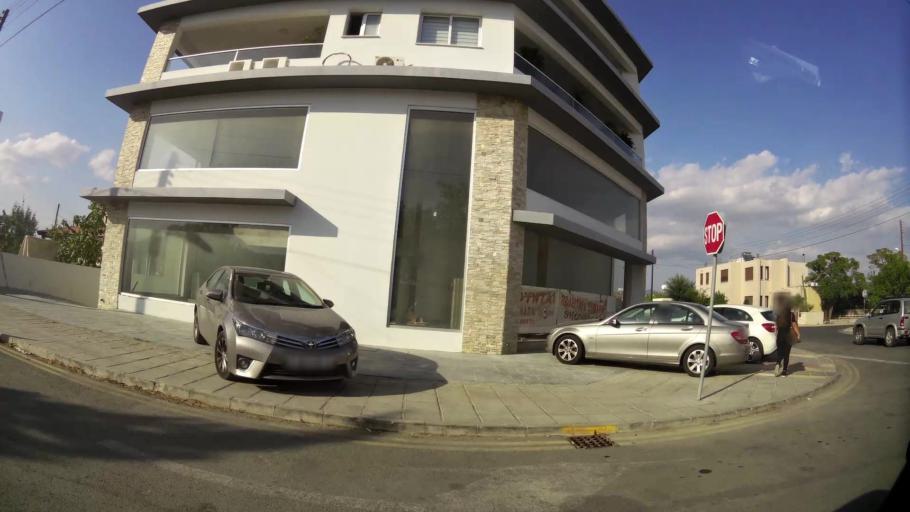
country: CY
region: Lefkosia
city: Nicosia
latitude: 35.1800
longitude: 33.3250
